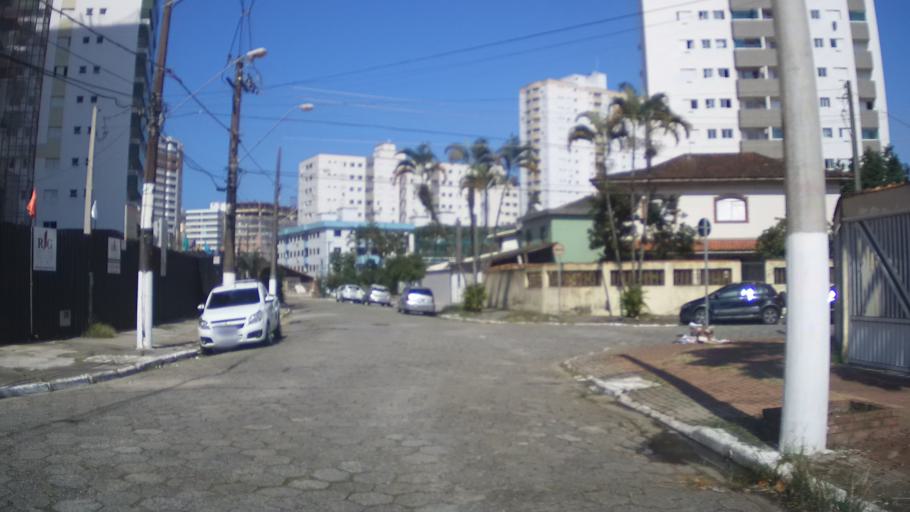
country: BR
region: Sao Paulo
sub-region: Praia Grande
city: Praia Grande
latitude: -24.0067
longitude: -46.4236
